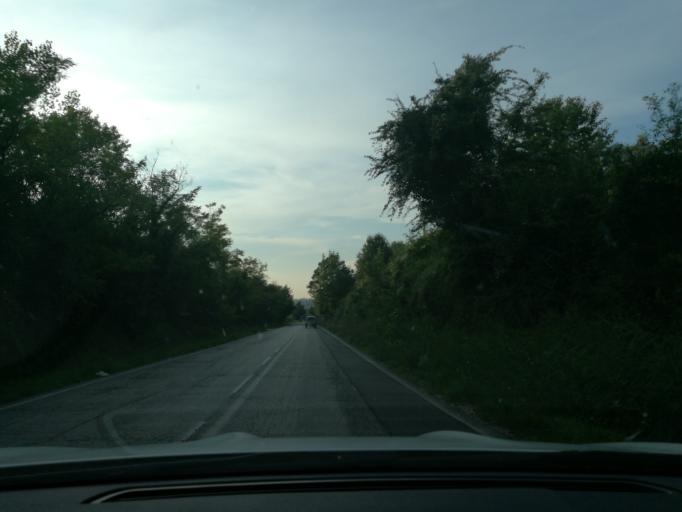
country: IT
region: Umbria
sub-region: Provincia di Terni
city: San Gemini
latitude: 42.6393
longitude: 12.5445
